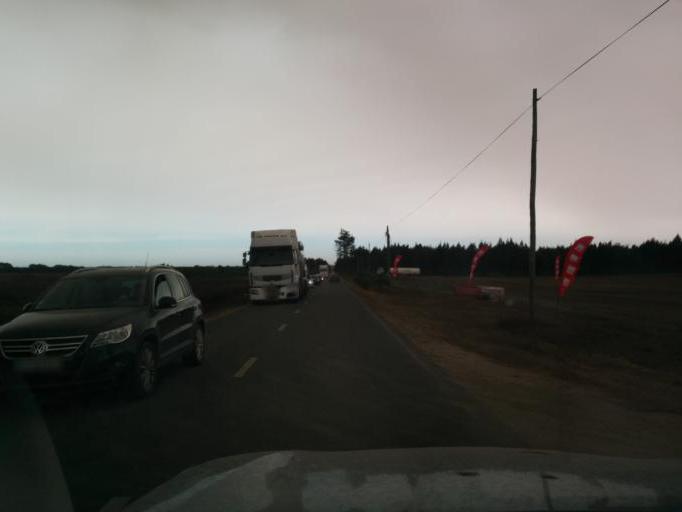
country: PT
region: Beja
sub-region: Odemira
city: Sao Teotonio
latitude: 37.5554
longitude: -8.7349
